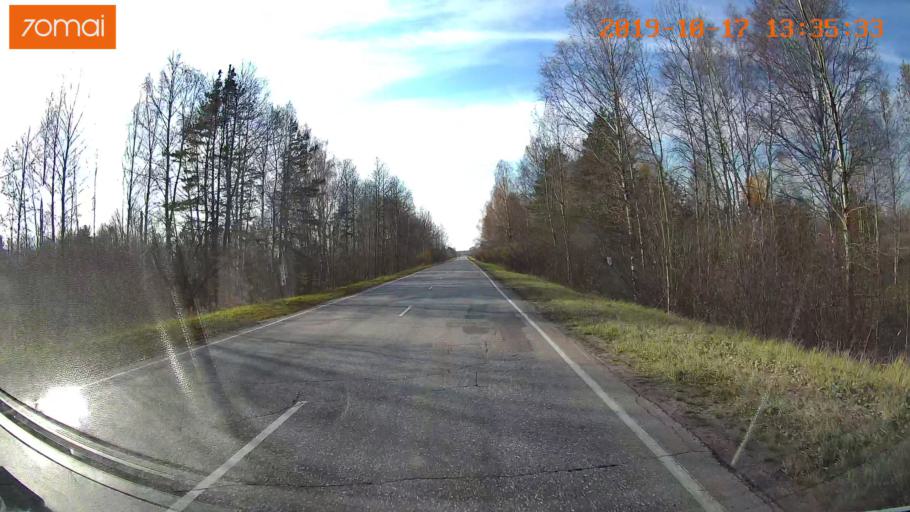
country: RU
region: Vladimir
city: Velikodvorskiy
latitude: 55.1420
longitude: 40.6866
